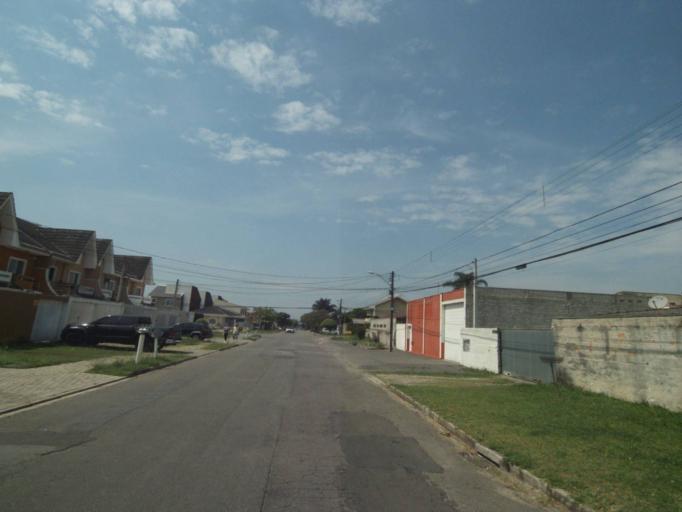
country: BR
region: Parana
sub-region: Pinhais
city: Pinhais
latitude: -25.4148
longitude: -49.2014
